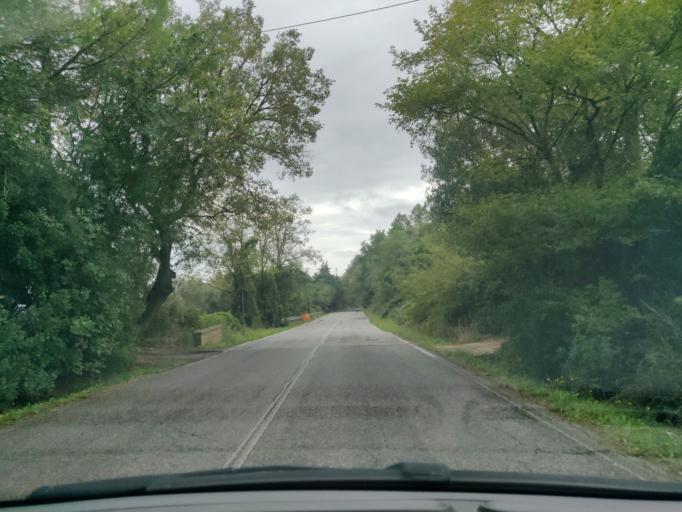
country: IT
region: Latium
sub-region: Citta metropolitana di Roma Capitale
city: Allumiere
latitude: 42.1301
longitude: 11.8667
